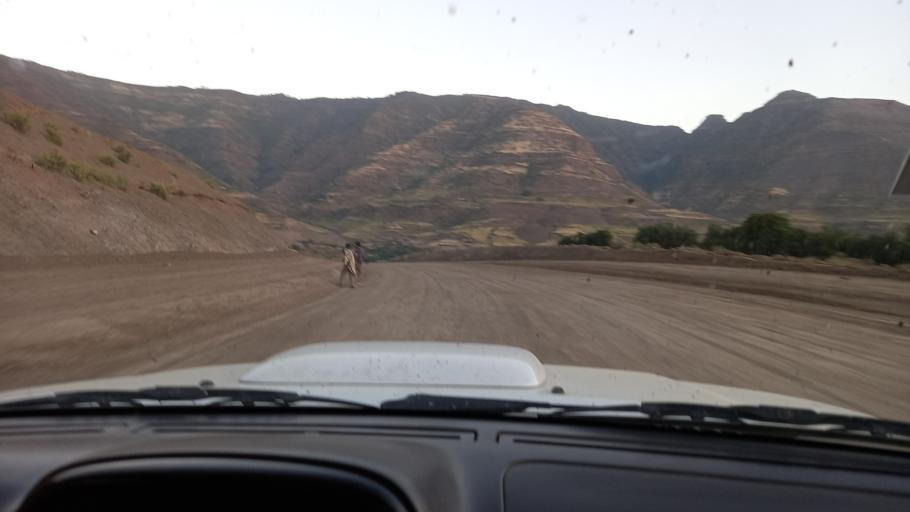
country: ET
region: Amhara
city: Debark'
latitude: 13.0364
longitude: 38.0414
